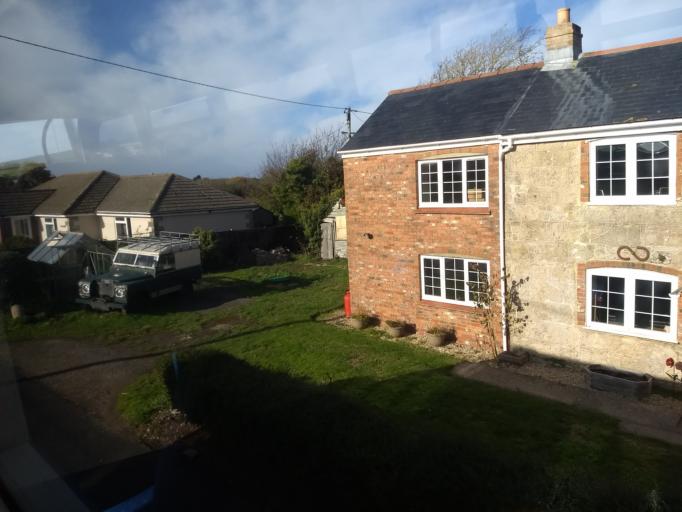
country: GB
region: England
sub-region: Isle of Wight
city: Shalfleet
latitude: 50.6926
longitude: -1.4338
